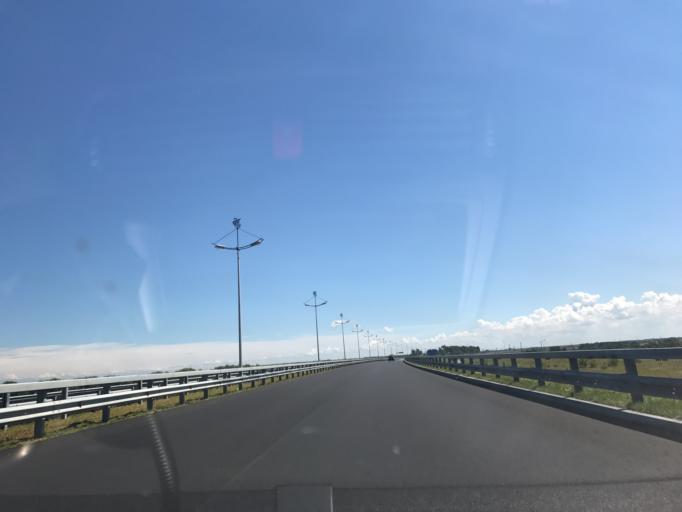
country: RU
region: Kaliningrad
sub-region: Zelenogradskiy Rayon
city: Zelenogradsk
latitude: 54.9168
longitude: 20.4813
